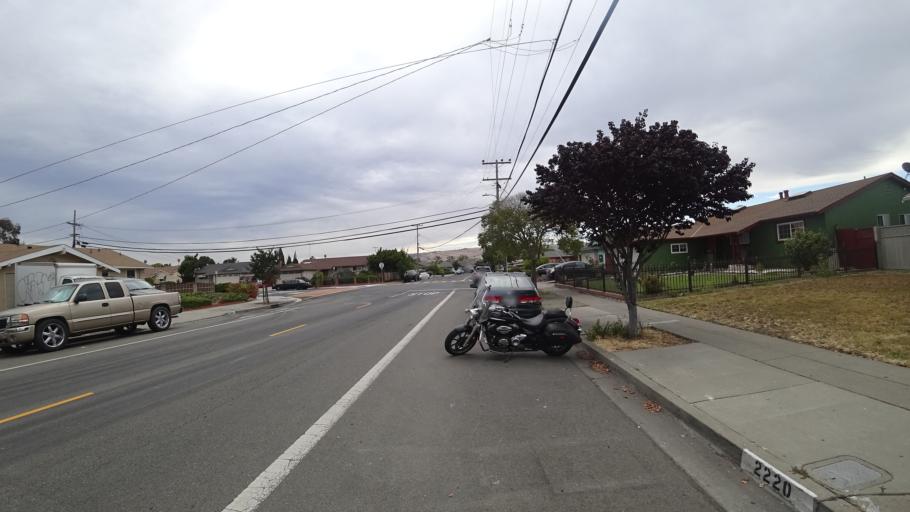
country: US
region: California
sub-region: Alameda County
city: Hayward
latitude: 37.6217
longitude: -122.0870
